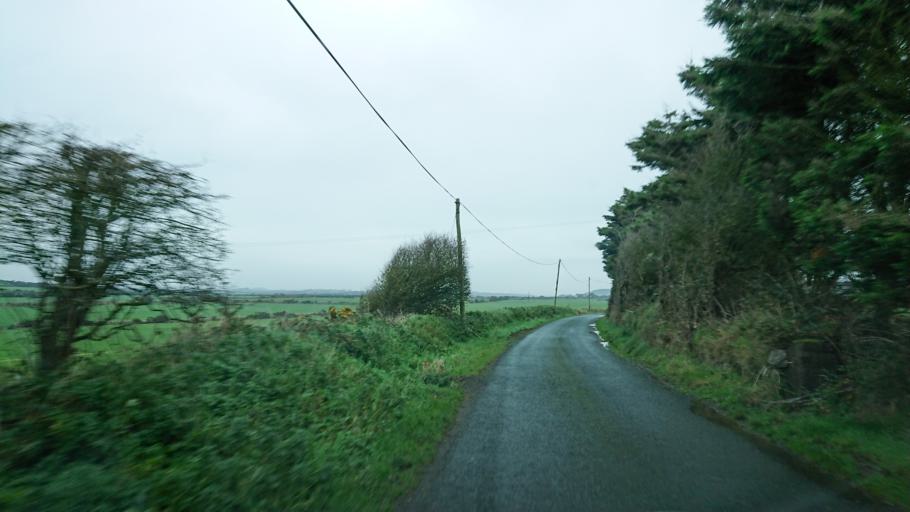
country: IE
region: Munster
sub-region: Waterford
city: Dunmore East
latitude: 52.1482
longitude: -7.0485
